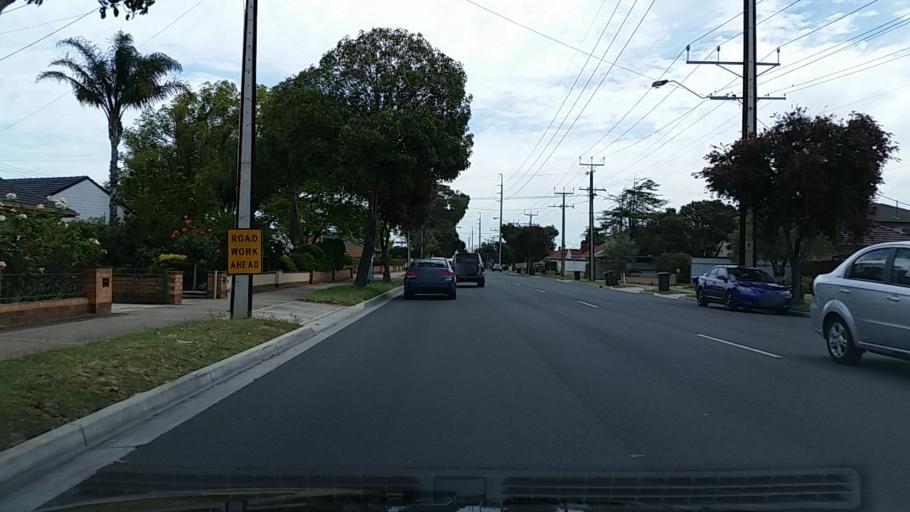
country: AU
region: South Australia
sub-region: Charles Sturt
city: Findon
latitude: -34.8993
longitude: 138.5321
